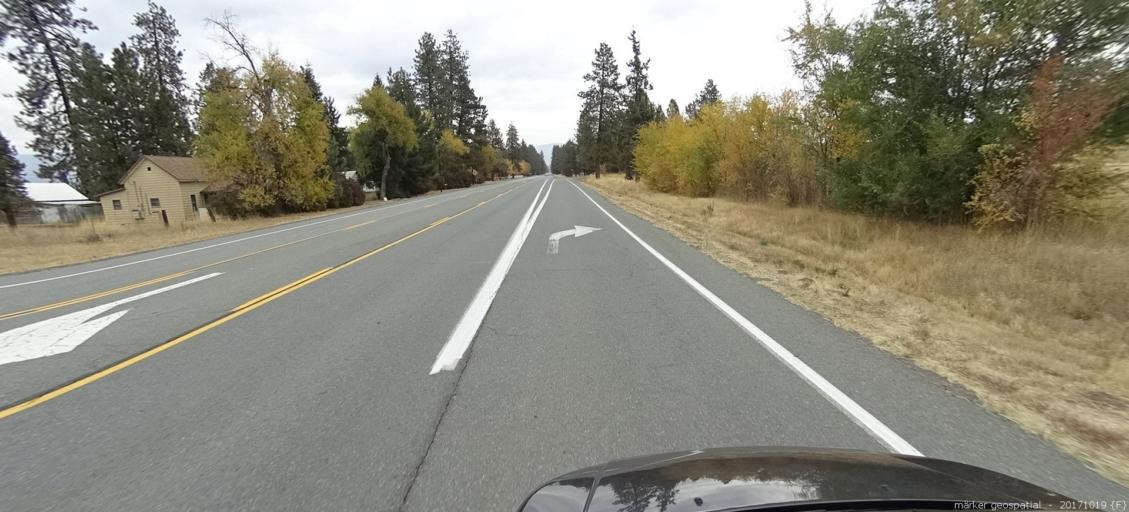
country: US
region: California
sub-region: Shasta County
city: Burney
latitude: 41.0583
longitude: -121.3776
